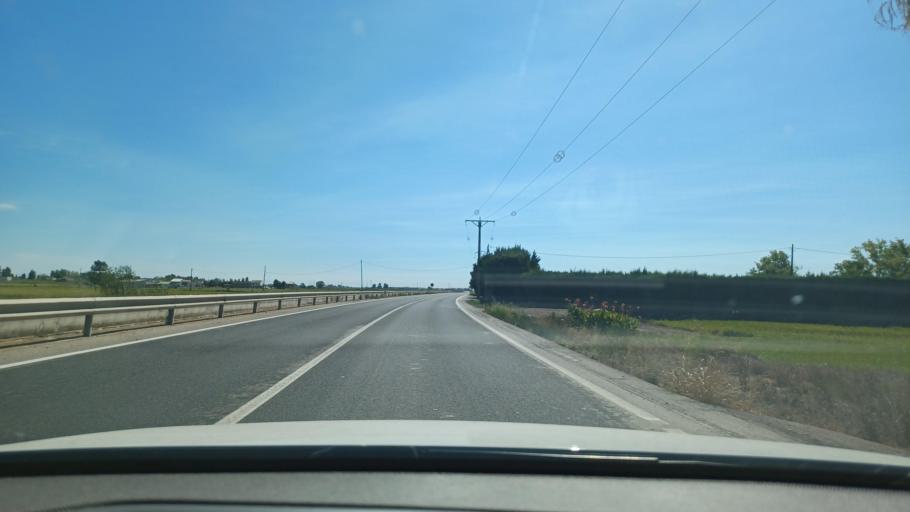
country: ES
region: Catalonia
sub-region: Provincia de Tarragona
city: Deltebre
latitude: 40.7104
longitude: 0.6764
